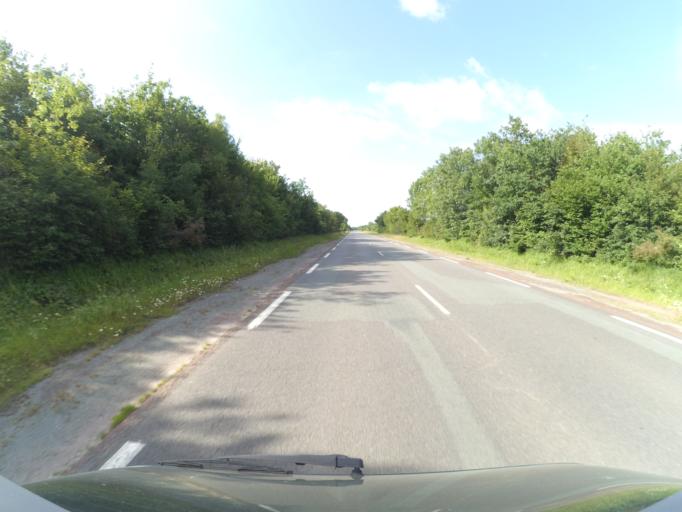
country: FR
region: Poitou-Charentes
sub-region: Departement de la Charente-Maritime
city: Le Gua
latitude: 45.7905
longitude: -0.9361
